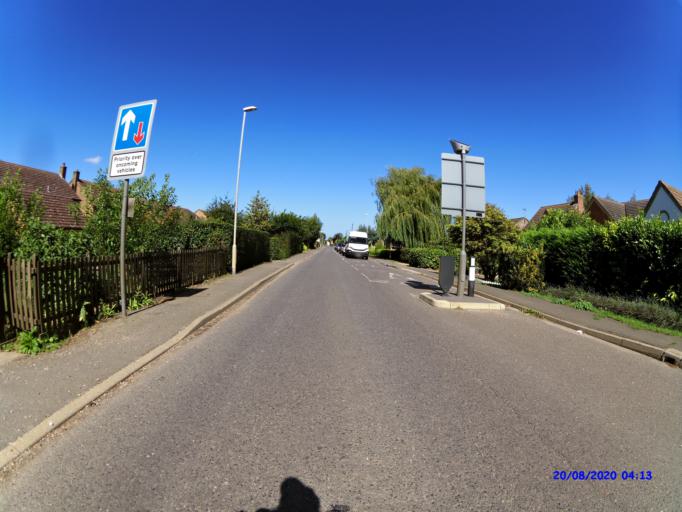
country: GB
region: England
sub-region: Cambridgeshire
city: Ramsey
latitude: 52.4831
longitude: -0.1062
